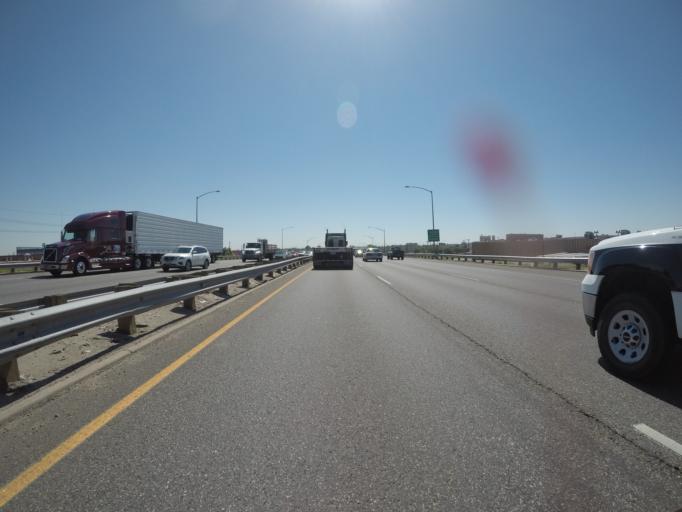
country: US
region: Colorado
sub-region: Adams County
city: Commerce City
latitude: 39.7799
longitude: -104.9314
